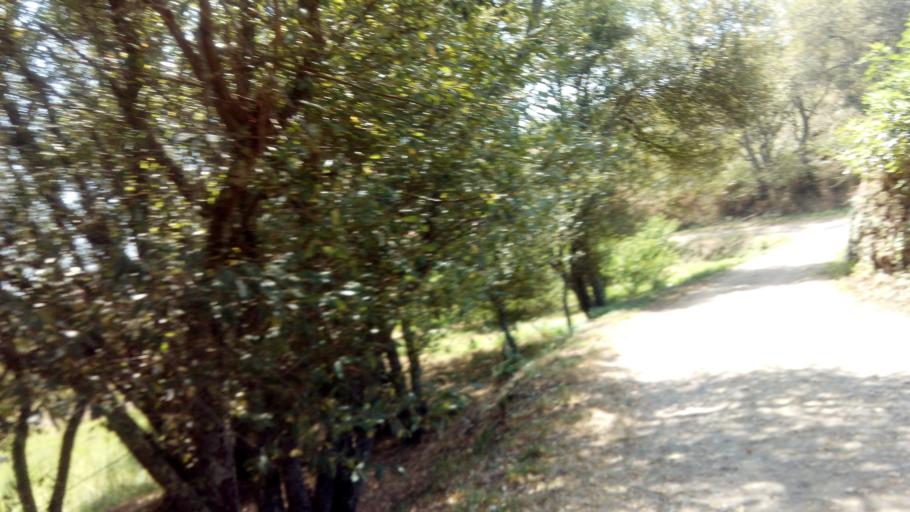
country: ES
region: Galicia
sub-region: Provincia de Pontevedra
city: Sanxenxo
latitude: 42.3779
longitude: -8.9328
